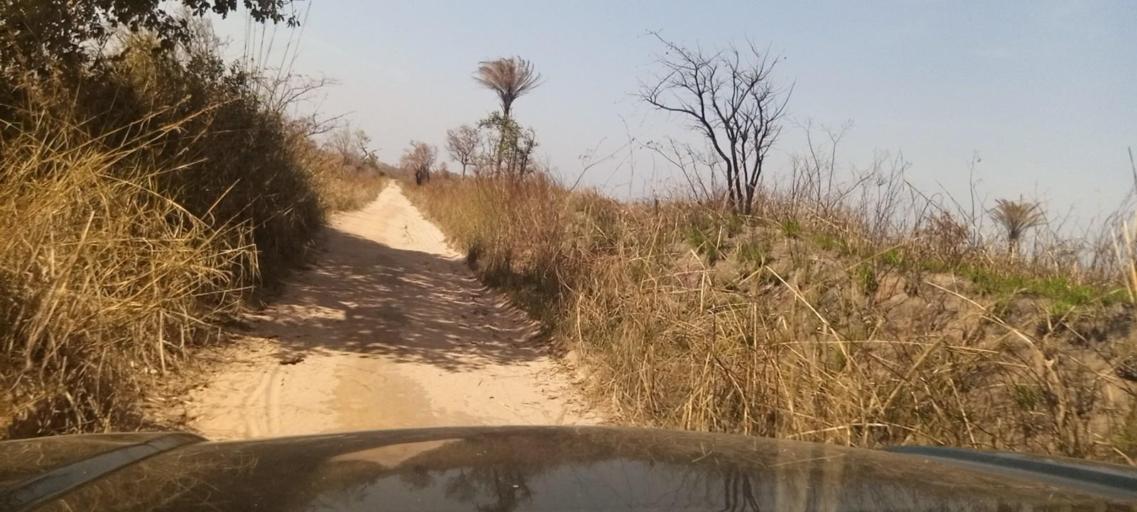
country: CD
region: Kasai-Oriental
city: Kabinda
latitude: -5.7951
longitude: 25.0318
